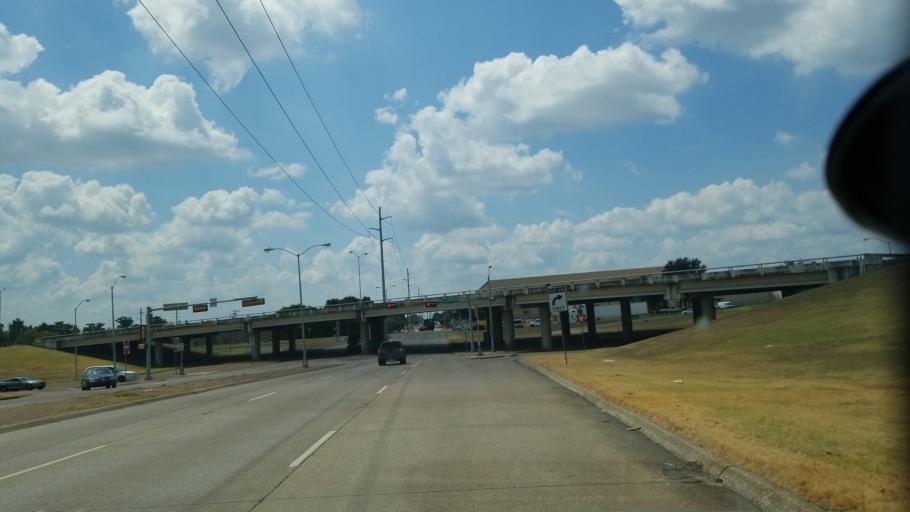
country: US
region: Texas
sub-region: Dallas County
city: Cockrell Hill
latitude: 32.6926
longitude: -96.8916
